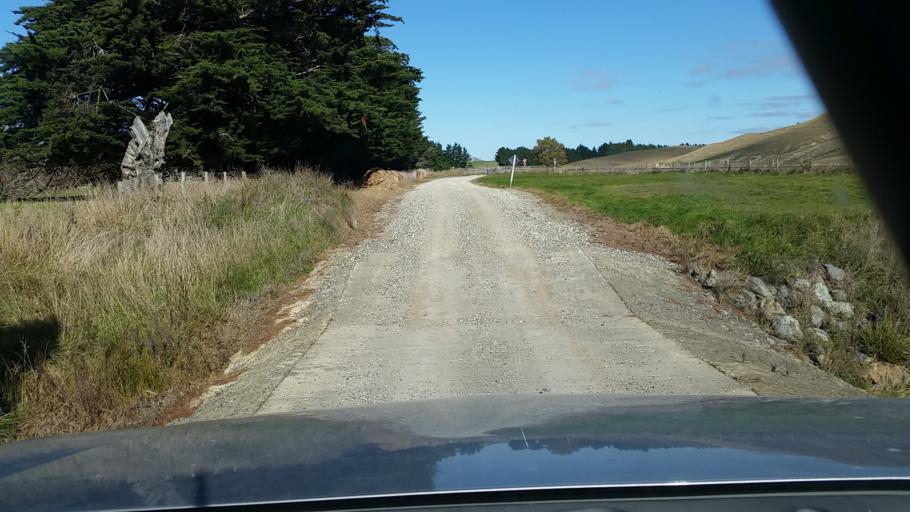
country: NZ
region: Marlborough
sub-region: Marlborough District
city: Blenheim
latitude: -41.7538
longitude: 174.1597
